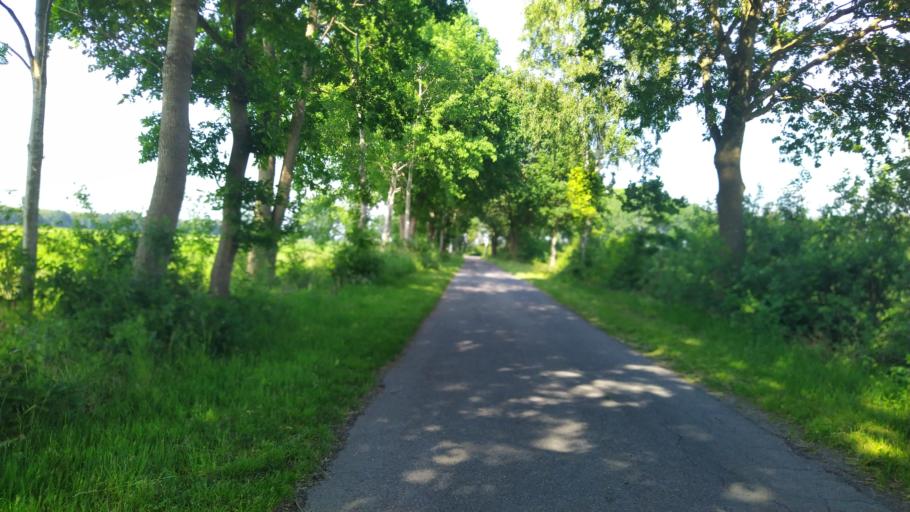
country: DE
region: Lower Saxony
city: Wohnste
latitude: 53.3924
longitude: 9.5528
